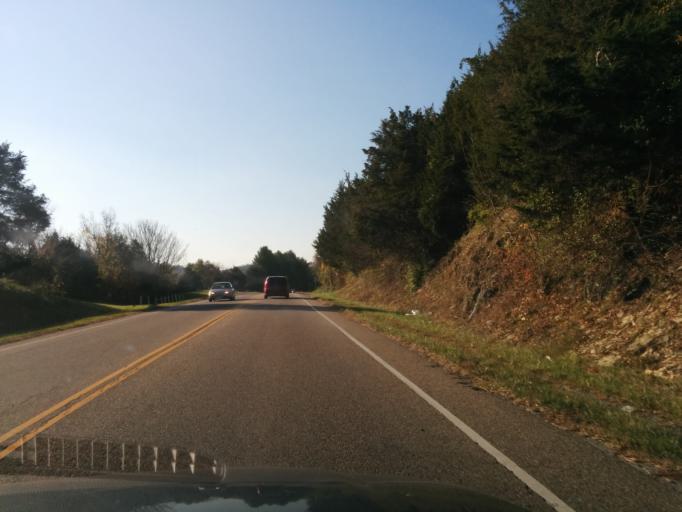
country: US
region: Virginia
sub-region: Rockbridge County
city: East Lexington
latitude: 37.7834
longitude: -79.4303
